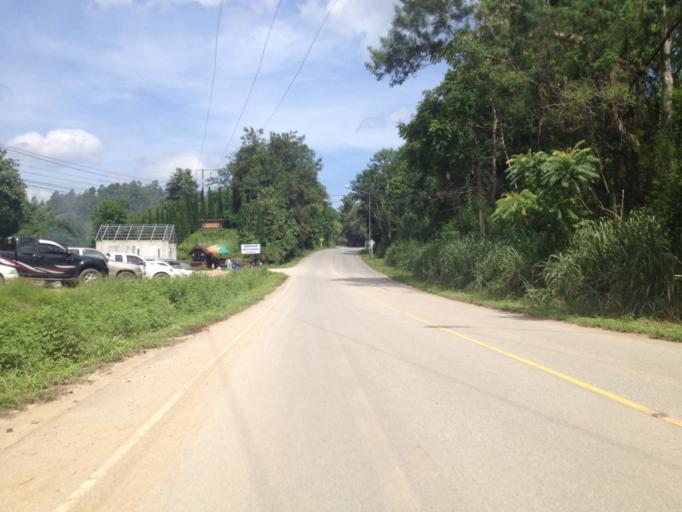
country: TH
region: Chiang Mai
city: Hang Dong
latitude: 18.7723
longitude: 98.8623
